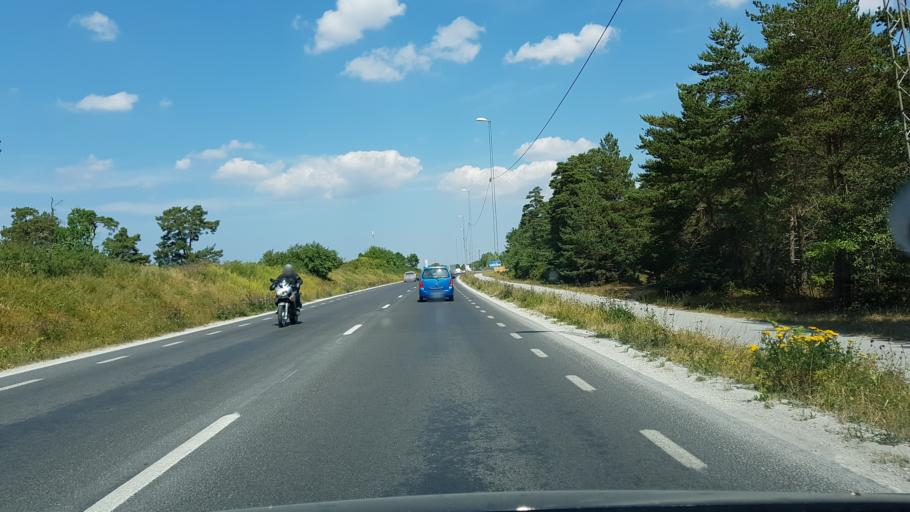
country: SE
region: Gotland
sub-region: Gotland
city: Visby
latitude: 57.6297
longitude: 18.3248
